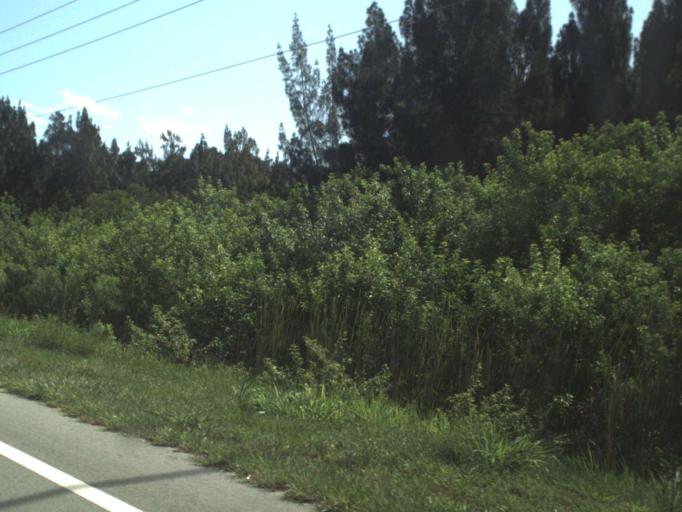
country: US
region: Florida
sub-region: Indian River County
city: Vero Beach
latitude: 27.6247
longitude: -80.3786
